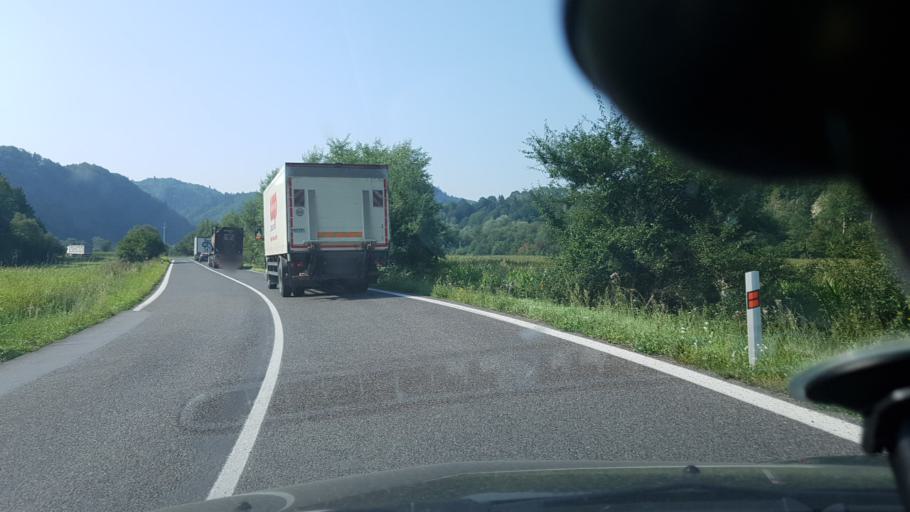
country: SK
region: Zilinsky
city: Tvrdosin
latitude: 49.2787
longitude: 19.4620
